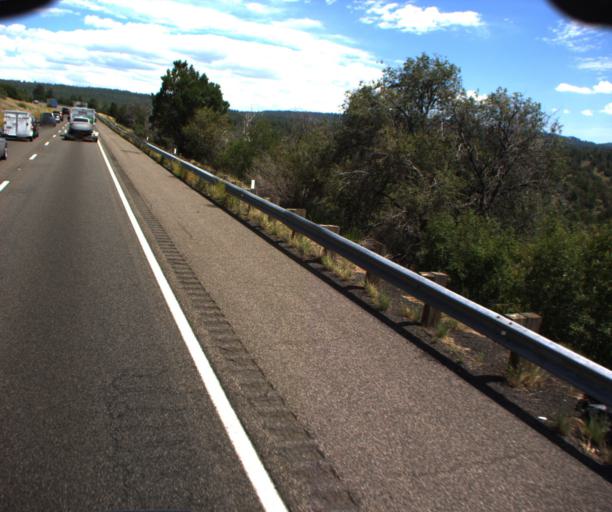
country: US
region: Arizona
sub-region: Yavapai County
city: Village of Oak Creek (Big Park)
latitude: 34.7925
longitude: -111.5904
